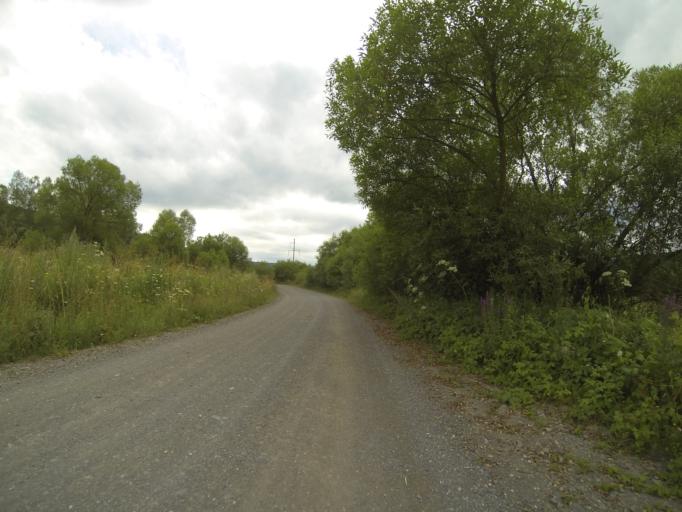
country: RO
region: Brasov
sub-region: Comuna Hoghiz
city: Hoghiz
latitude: 46.0049
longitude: 25.3853
